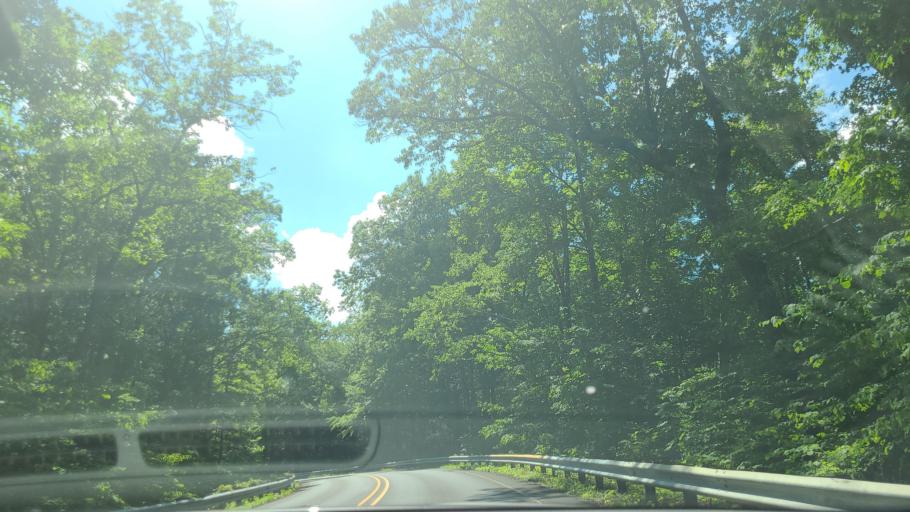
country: US
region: Kentucky
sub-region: Whitley County
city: Williamsburg
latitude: 36.8437
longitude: -84.3212
